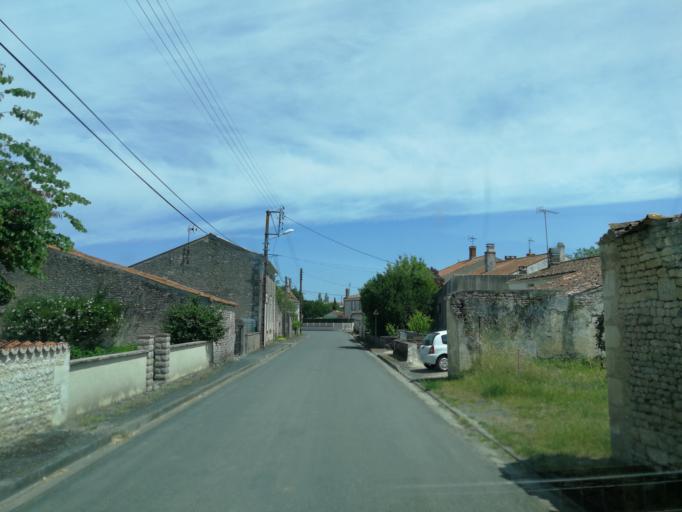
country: FR
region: Pays de la Loire
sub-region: Departement de la Vendee
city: Le Langon
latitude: 46.4173
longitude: -0.9089
